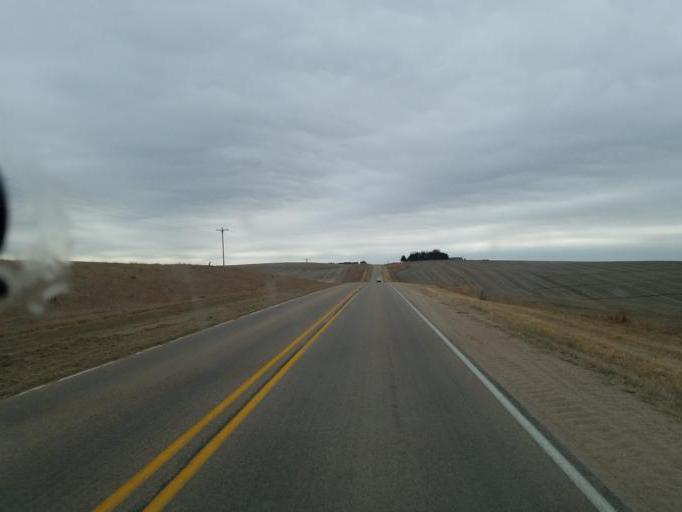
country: US
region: Nebraska
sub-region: Cedar County
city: Hartington
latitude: 42.4883
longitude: -97.2113
